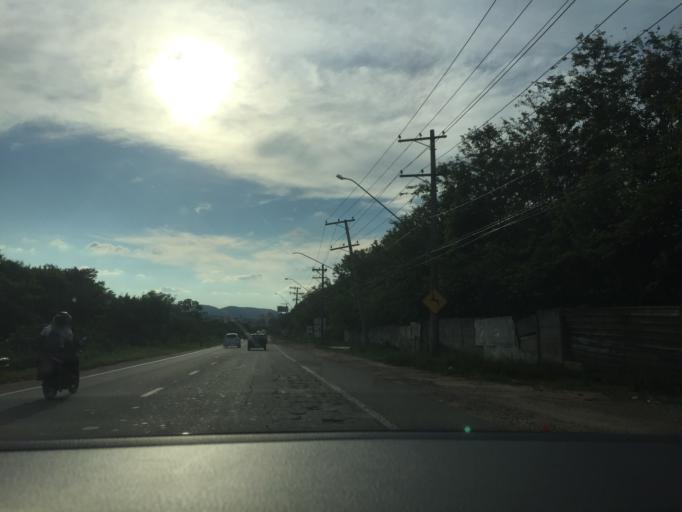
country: BR
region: Sao Paulo
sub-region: Varzea Paulista
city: Varzea Paulista
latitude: -23.2014
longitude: -46.8431
